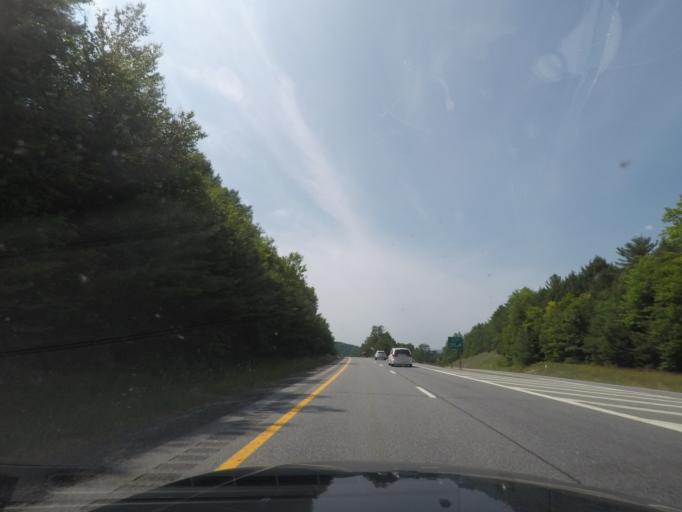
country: US
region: New York
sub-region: Warren County
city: Warrensburg
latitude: 43.6661
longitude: -73.7733
